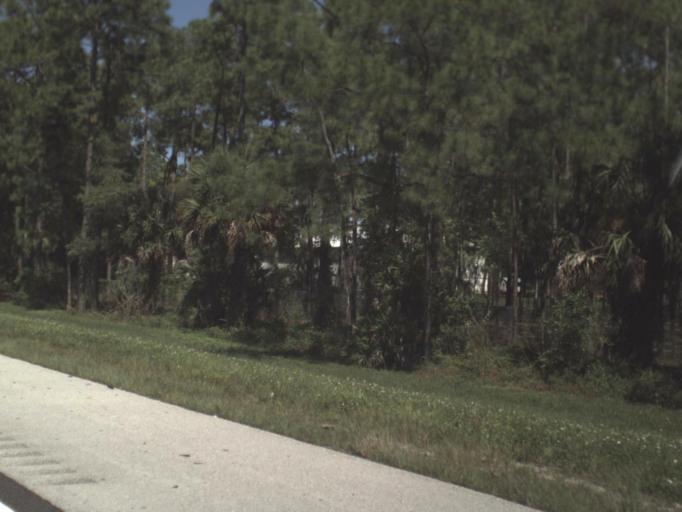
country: US
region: Florida
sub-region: Collier County
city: Vineyards
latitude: 26.2488
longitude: -81.7376
